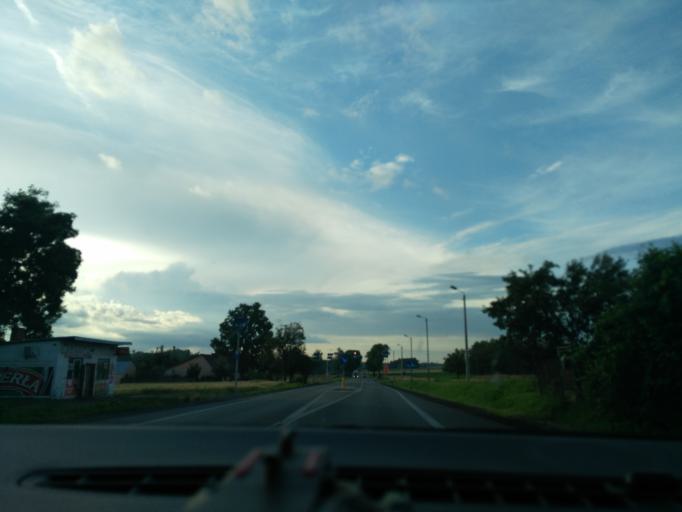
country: PL
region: Lublin Voivodeship
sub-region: Powiat lubelski
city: Niedrzwica Duza
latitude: 51.0761
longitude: 22.3751
